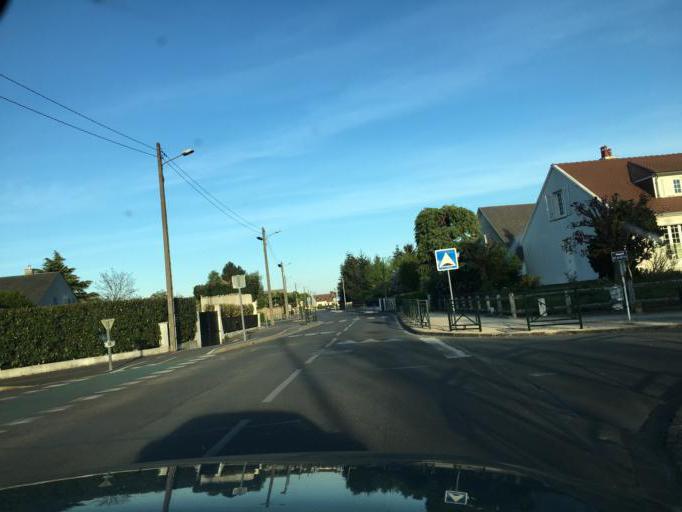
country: FR
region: Centre
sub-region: Departement du Loiret
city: Saint-Jean-le-Blanc
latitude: 47.8830
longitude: 1.9352
